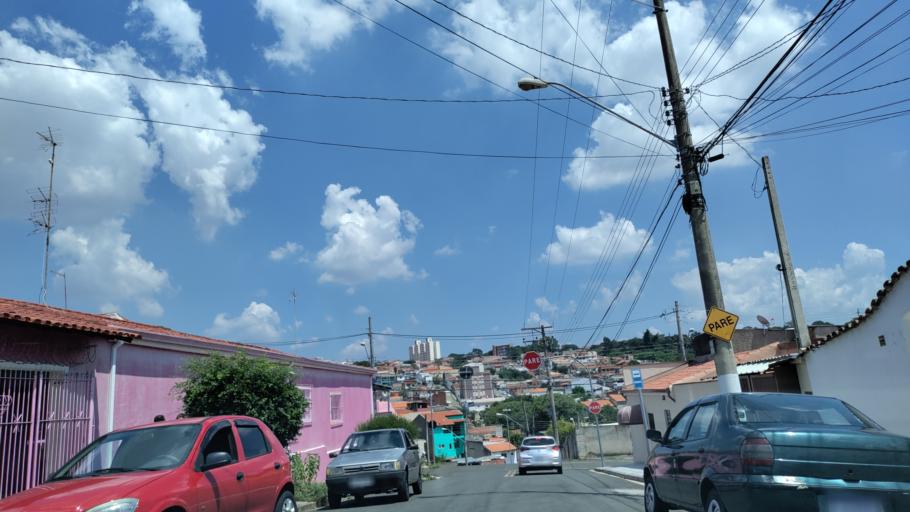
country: BR
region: Sao Paulo
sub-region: Sorocaba
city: Sorocaba
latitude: -23.4841
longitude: -47.4596
